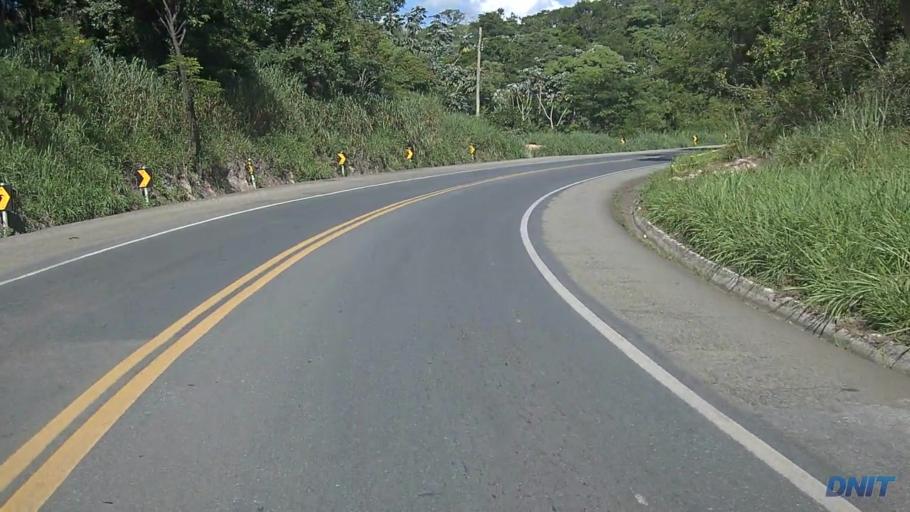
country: BR
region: Minas Gerais
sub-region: Barao De Cocais
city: Barao de Cocais
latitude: -19.8045
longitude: -43.4036
